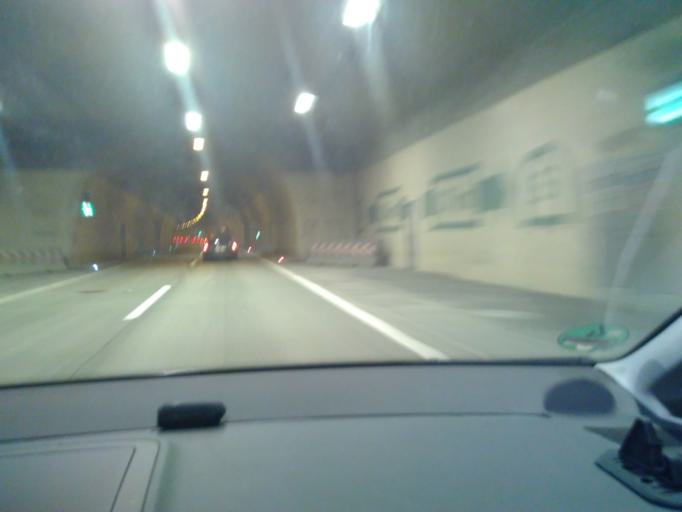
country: AT
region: Salzburg
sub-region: Politischer Bezirk Hallein
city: Golling an der Salzach
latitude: 47.5705
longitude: 13.1695
